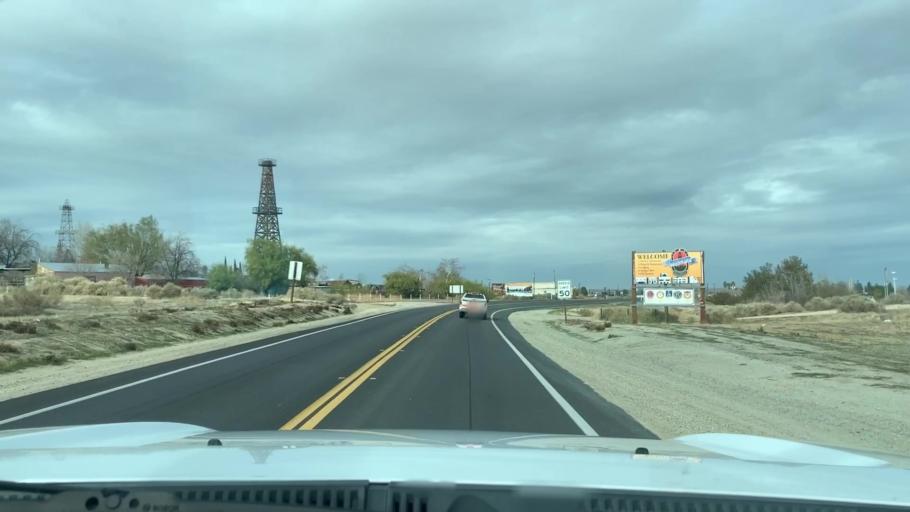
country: US
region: California
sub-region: Kern County
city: South Taft
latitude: 35.1323
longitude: -119.4462
